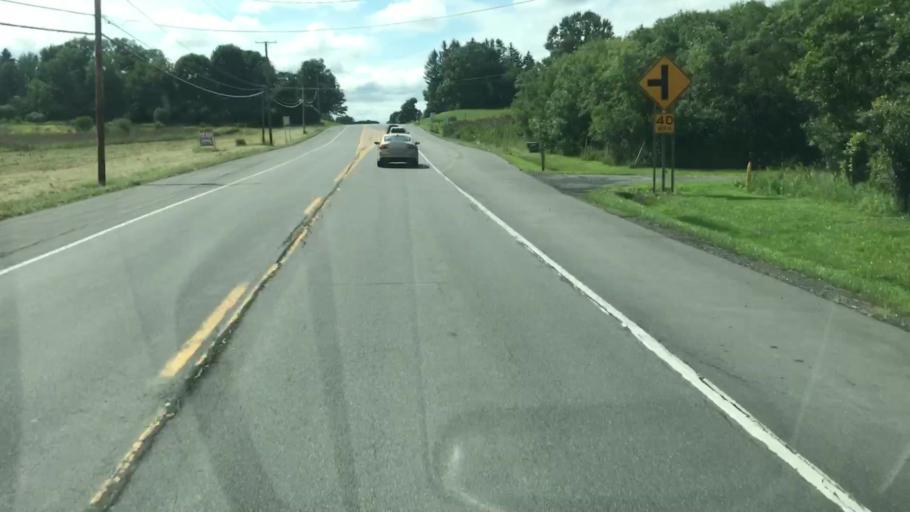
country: US
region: New York
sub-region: Cayuga County
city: Melrose Park
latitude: 42.9367
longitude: -76.5224
